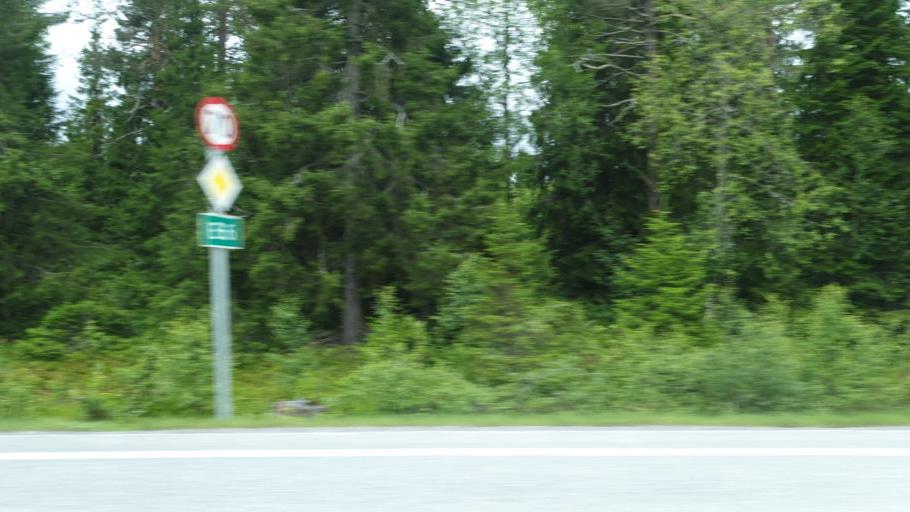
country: NO
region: Sor-Trondelag
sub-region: Rennebu
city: Berkak
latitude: 62.8890
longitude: 10.1012
